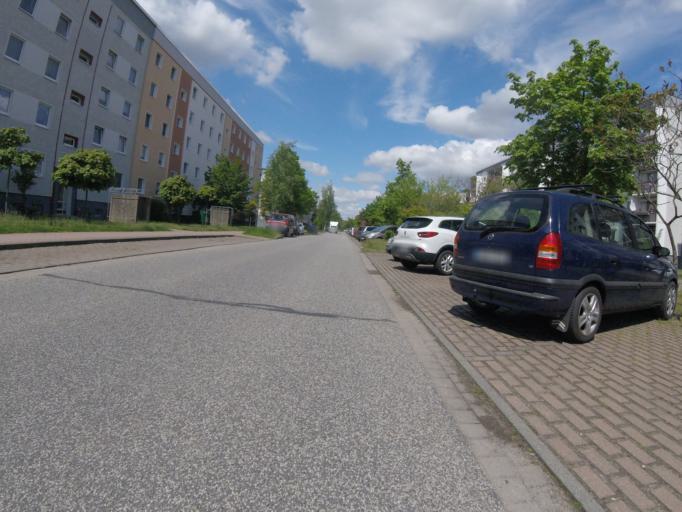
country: DE
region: Brandenburg
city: Konigs Wusterhausen
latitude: 52.2860
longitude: 13.6123
